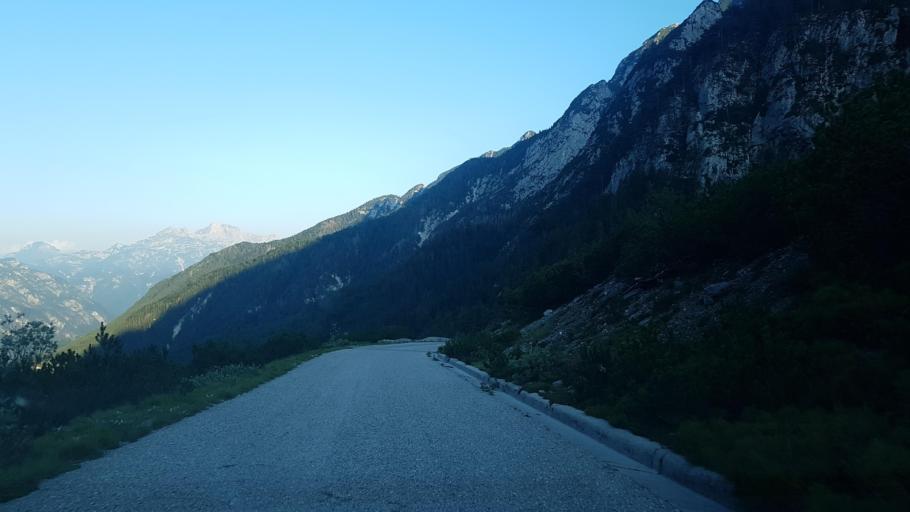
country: IT
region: Friuli Venezia Giulia
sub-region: Provincia di Udine
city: Malborghetto
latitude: 46.4631
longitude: 13.4348
